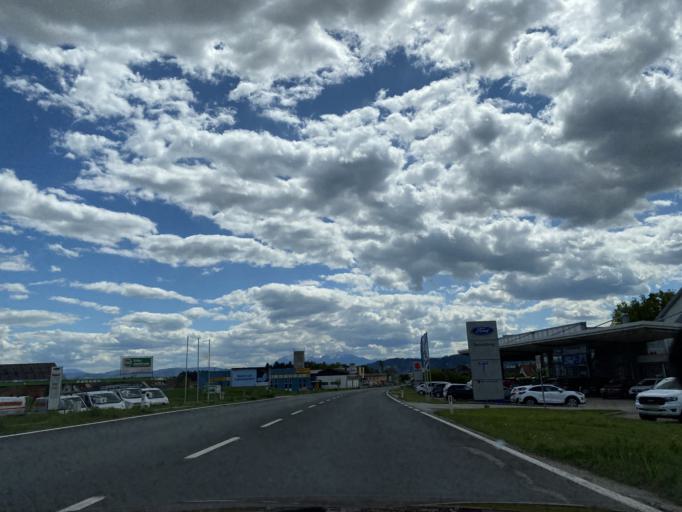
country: AT
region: Carinthia
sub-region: Politischer Bezirk Wolfsberg
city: Wolfsberg
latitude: 46.8161
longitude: 14.8352
